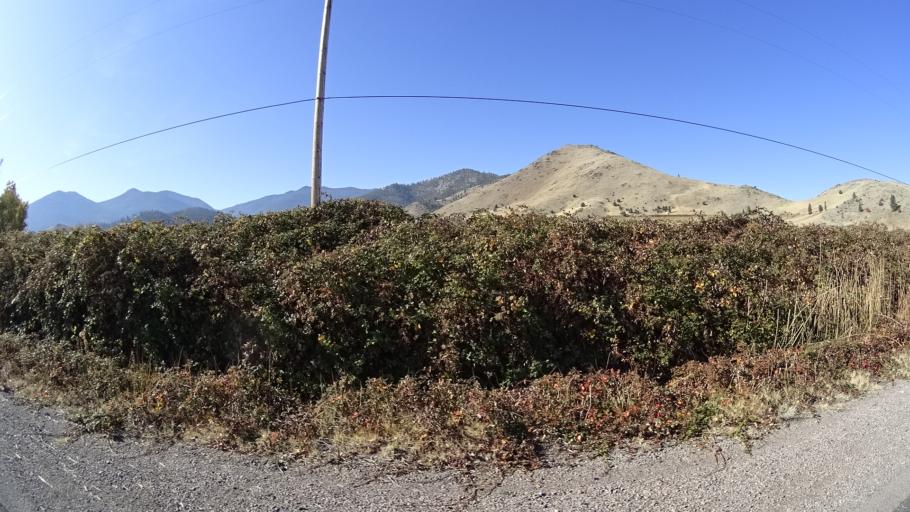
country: US
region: California
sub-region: Siskiyou County
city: Weed
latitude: 41.4599
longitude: -122.4625
